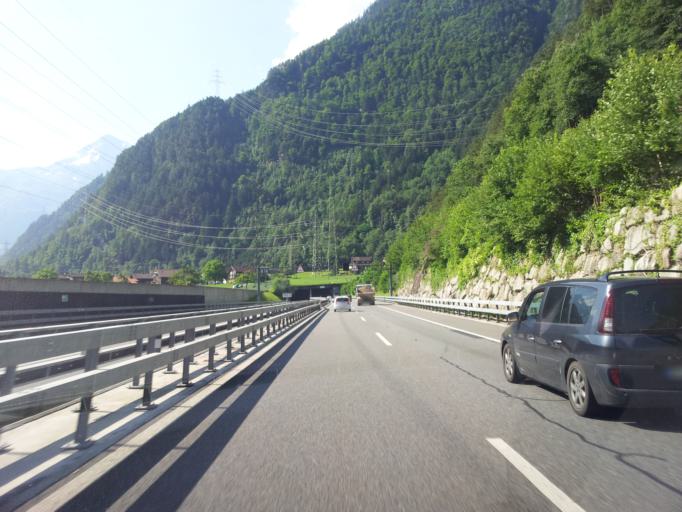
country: CH
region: Uri
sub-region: Uri
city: Erstfeld
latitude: 46.8227
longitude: 8.6418
